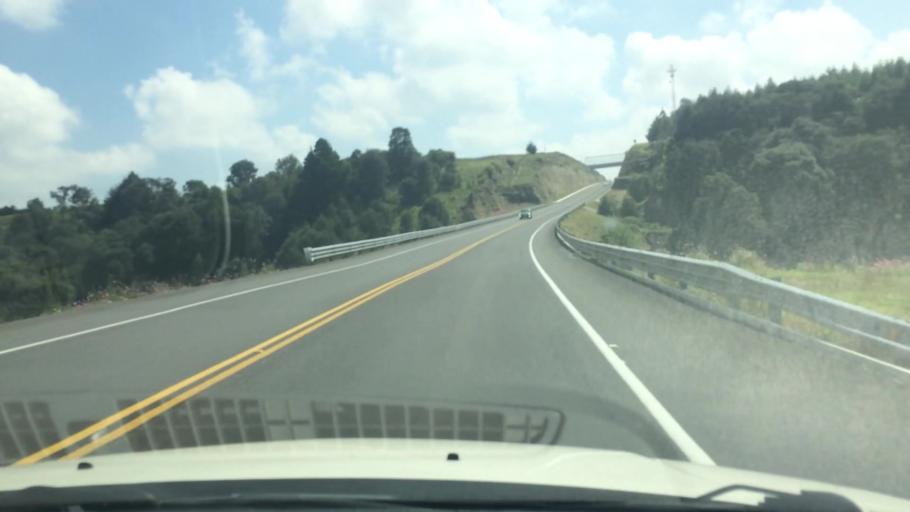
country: MX
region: Mexico
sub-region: Villa Victoria
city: Colonia Doctor Gustavo Baz
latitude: 19.3765
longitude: -99.9053
